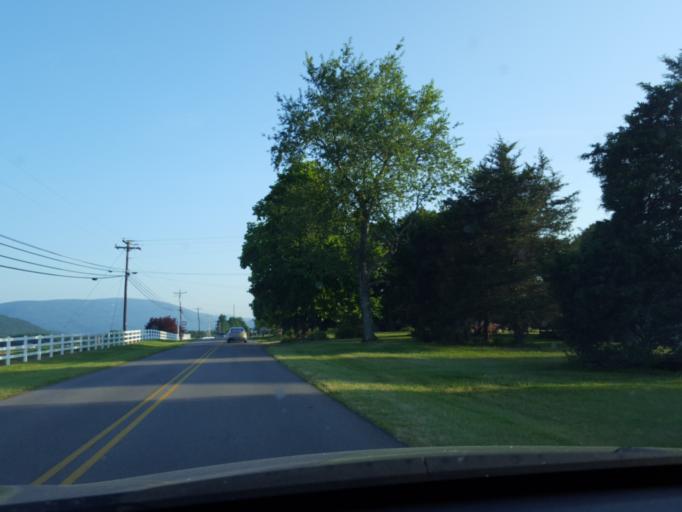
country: US
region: Virginia
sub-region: Augusta County
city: Lyndhurst
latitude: 38.0195
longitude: -78.9469
